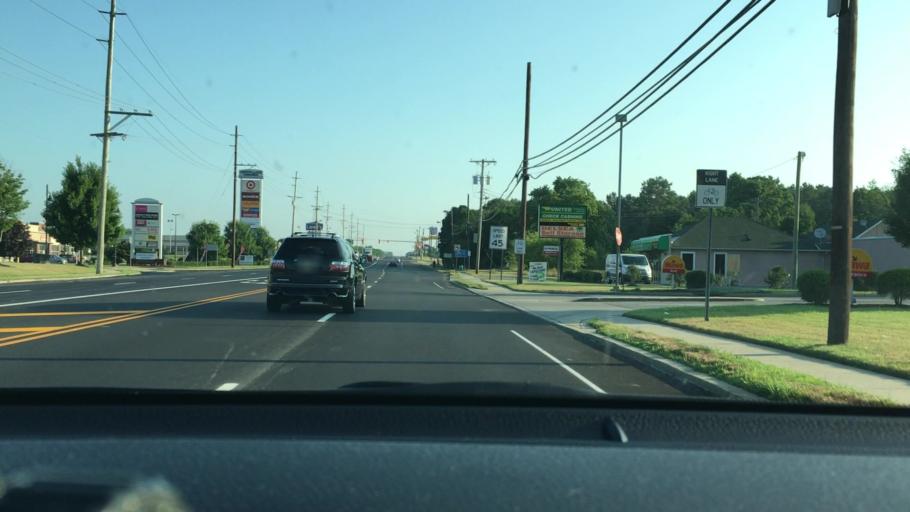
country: US
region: New Jersey
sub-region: Cumberland County
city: Millville
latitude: 39.4216
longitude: -75.0394
